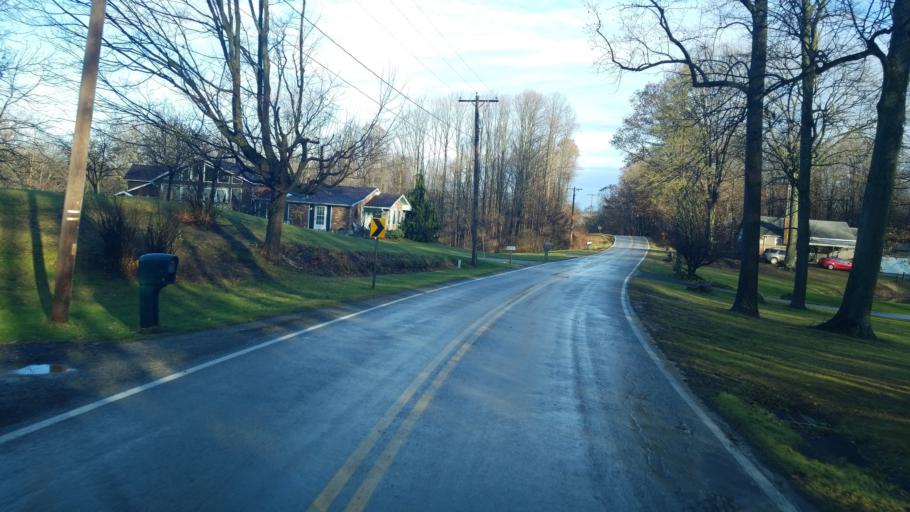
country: US
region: Ohio
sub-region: Richland County
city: Mansfield
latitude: 40.7170
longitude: -82.4893
